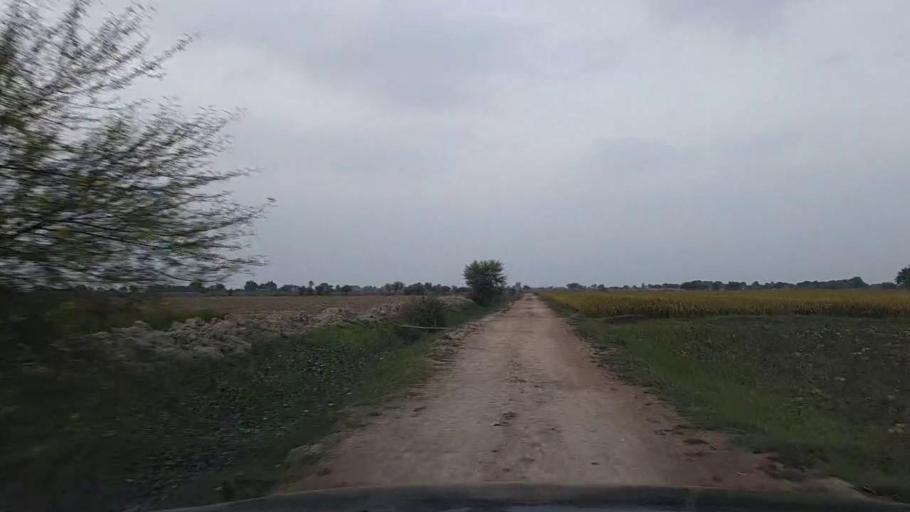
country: PK
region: Sindh
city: Jati
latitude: 24.5061
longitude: 68.3931
